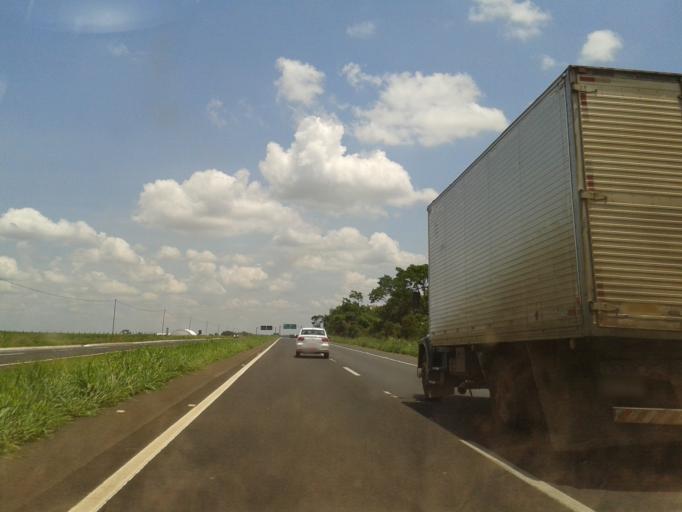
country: BR
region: Minas Gerais
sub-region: Monte Alegre De Minas
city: Monte Alegre de Minas
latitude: -18.8889
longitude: -48.6257
